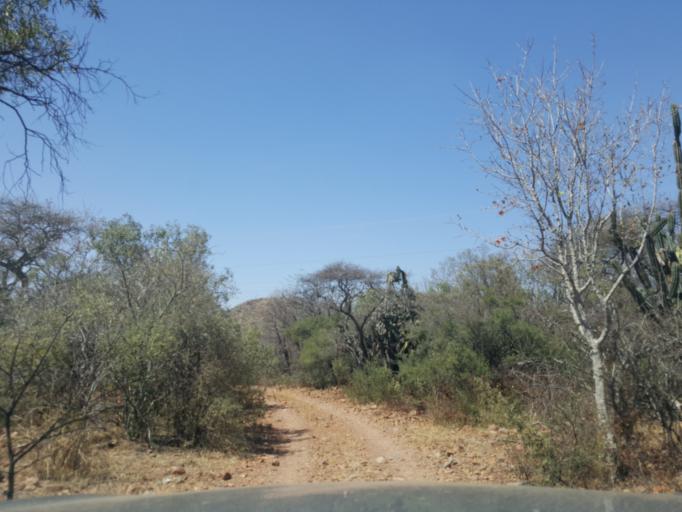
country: BW
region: South East
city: Lobatse
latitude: -25.1581
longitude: 25.6840
